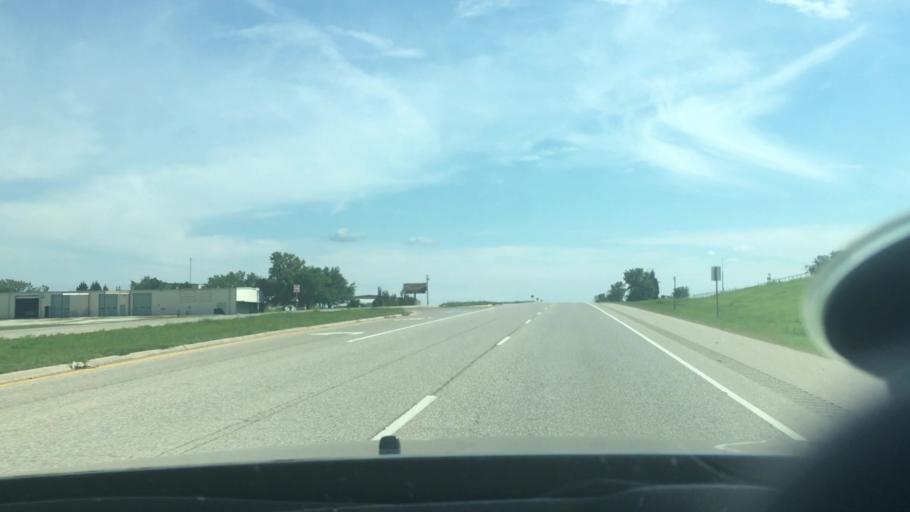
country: US
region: Oklahoma
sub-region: Seminole County
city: Seminole
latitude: 35.1989
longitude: -96.6751
